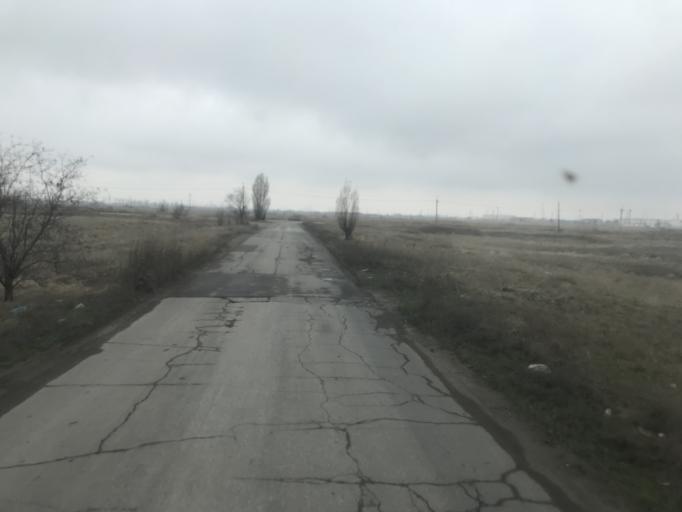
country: RU
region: Volgograd
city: Svetlyy Yar
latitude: 48.5008
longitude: 44.6453
